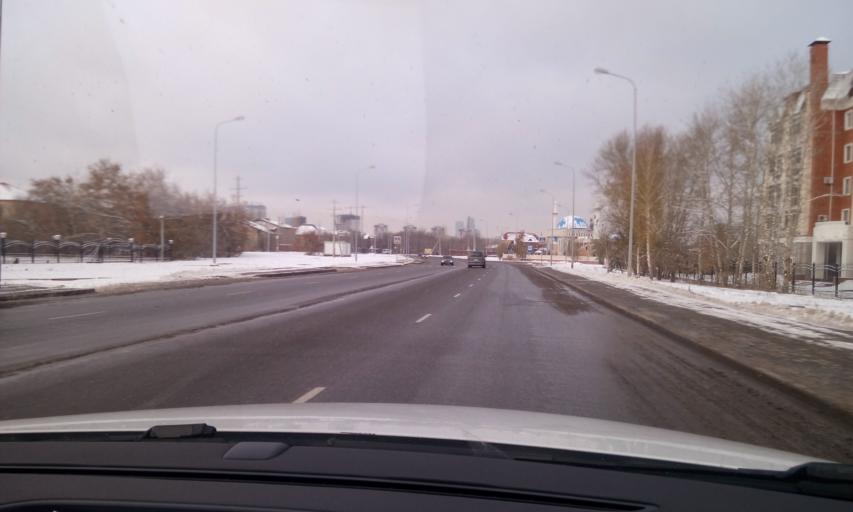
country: KZ
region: Astana Qalasy
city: Astana
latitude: 51.1368
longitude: 71.4354
